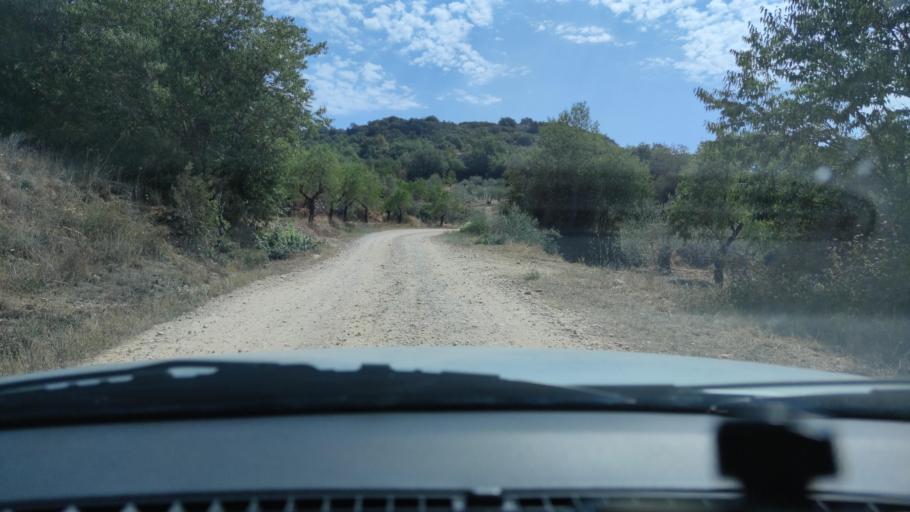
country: ES
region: Catalonia
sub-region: Provincia de Lleida
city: Ager
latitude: 41.9322
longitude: 0.8048
